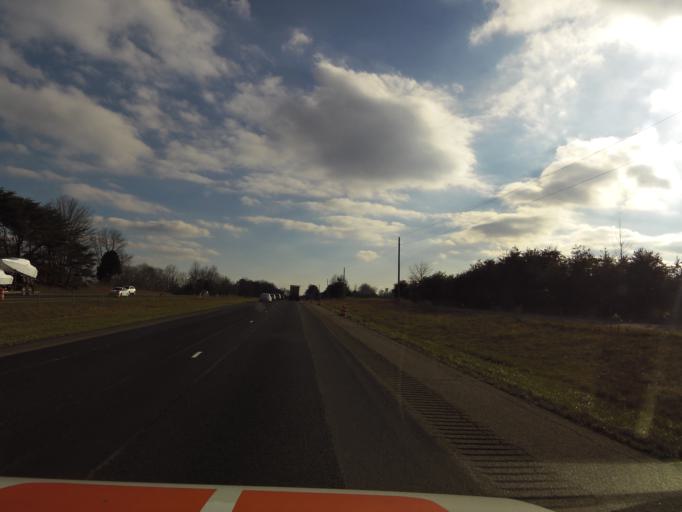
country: US
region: Indiana
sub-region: Clark County
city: Henryville
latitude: 38.6013
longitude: -85.7811
